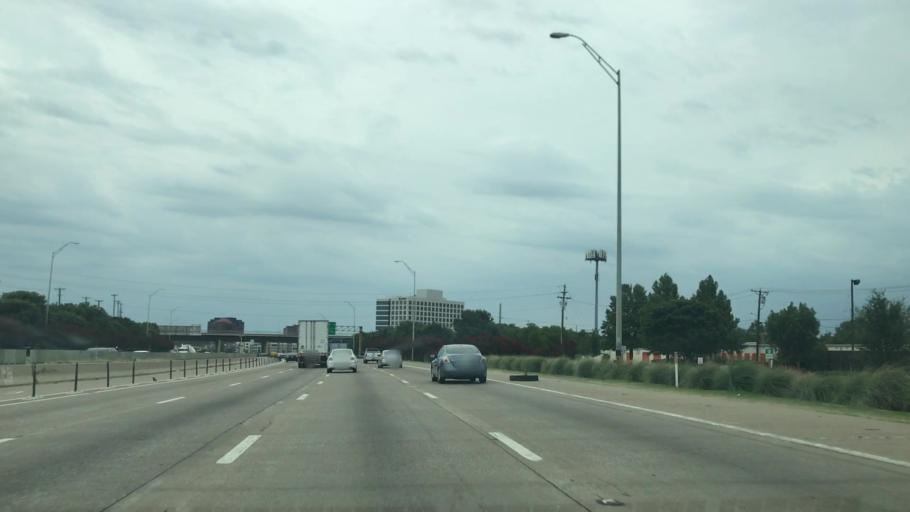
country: US
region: Texas
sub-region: Dallas County
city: Richardson
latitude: 32.9640
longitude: -96.7239
